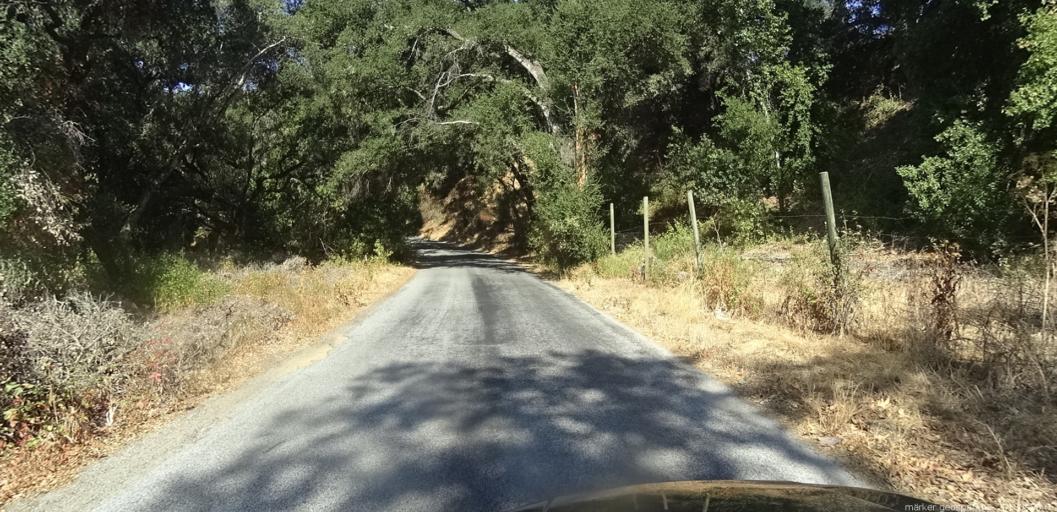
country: US
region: California
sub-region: Monterey County
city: Carmel Valley Village
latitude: 36.4087
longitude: -121.6657
